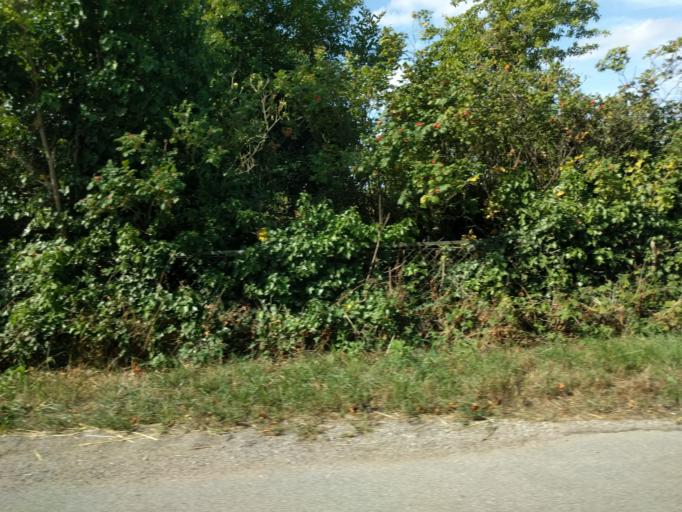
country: DK
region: Zealand
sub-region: Vordingborg Kommune
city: Stege
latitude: 54.9654
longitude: 12.2954
